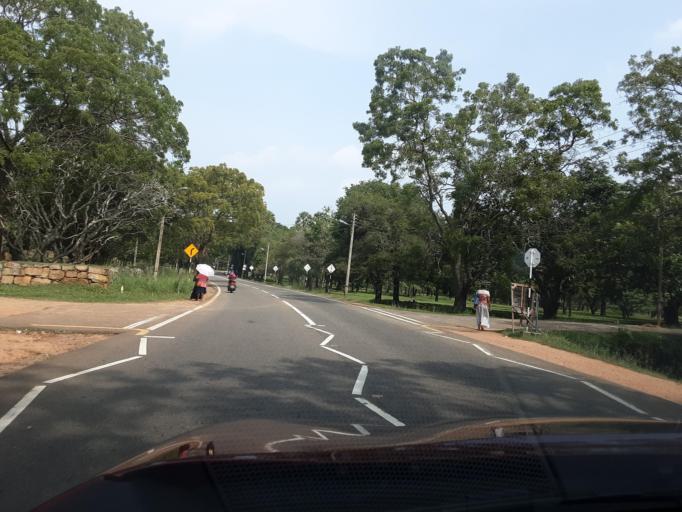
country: LK
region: North Central
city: Anuradhapura
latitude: 8.3523
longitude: 80.5096
